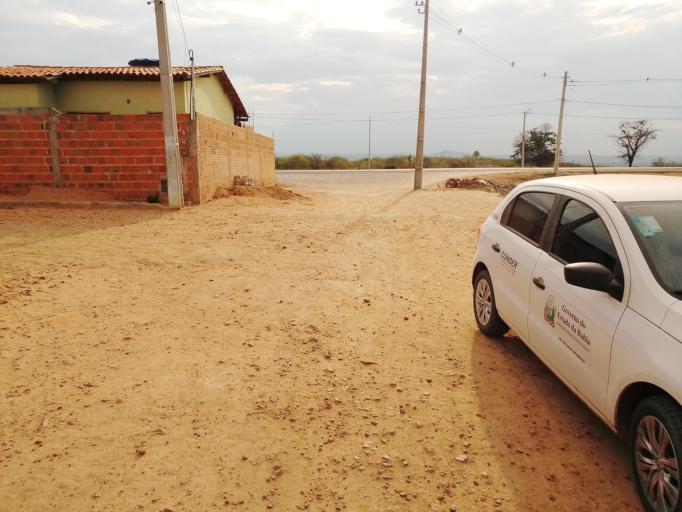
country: BR
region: Bahia
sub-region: Brumado
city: Brumado
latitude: -14.4413
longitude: -41.4637
